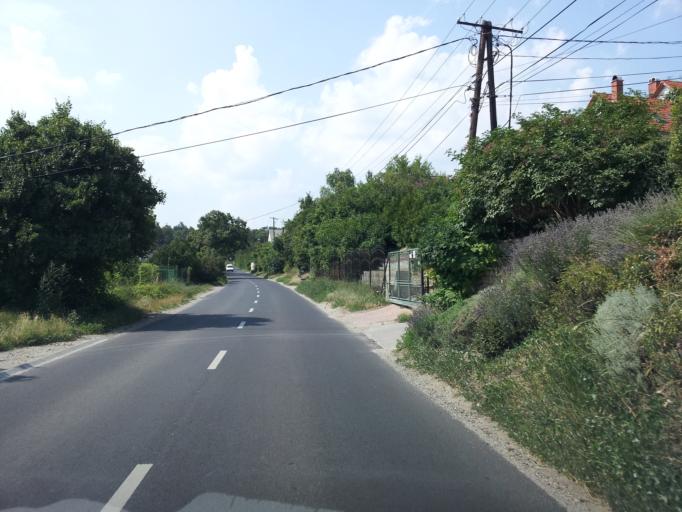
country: HU
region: Veszprem
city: Balatonfured
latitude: 46.9616
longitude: 17.8581
